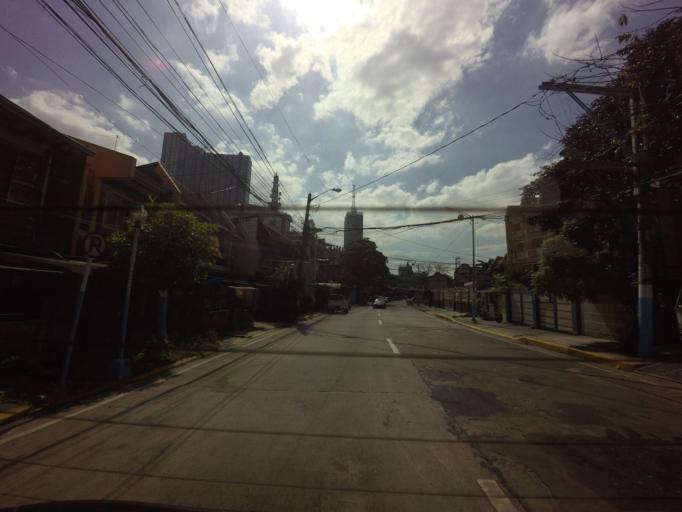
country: PH
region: Metro Manila
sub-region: City of Manila
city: Manila
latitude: 14.6193
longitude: 120.9979
